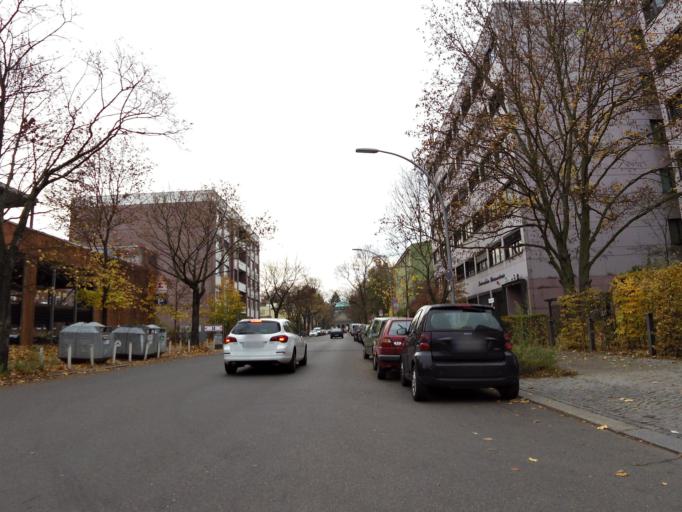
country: DE
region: Berlin
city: Schoneberg Bezirk
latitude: 52.4617
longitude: 13.3666
